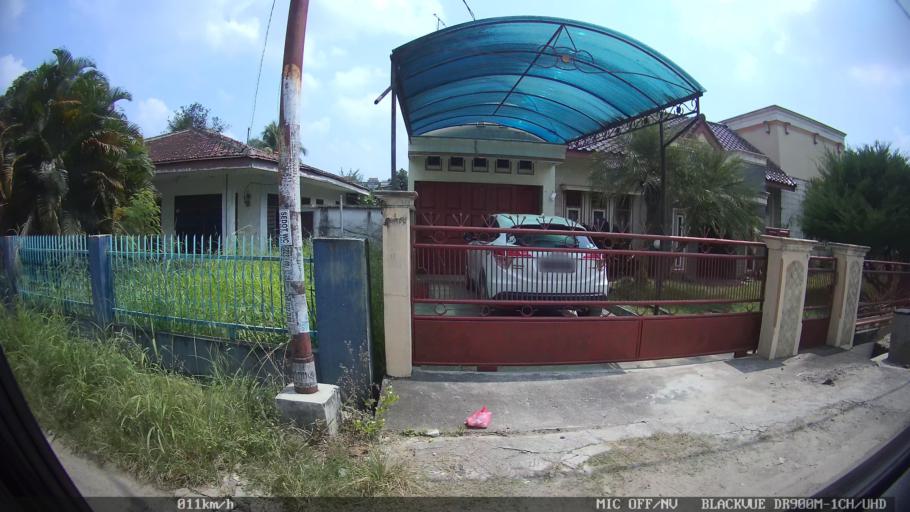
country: ID
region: Lampung
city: Pringsewu
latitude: -5.3583
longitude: 104.9816
